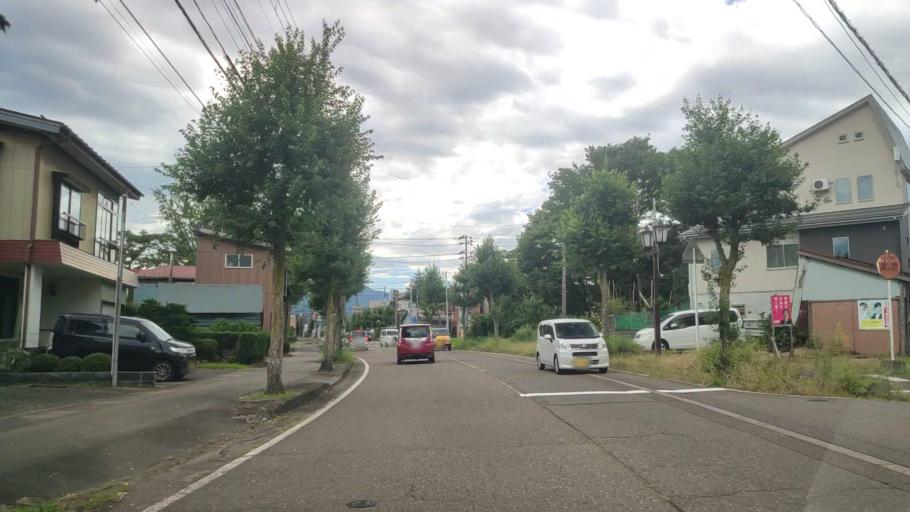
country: JP
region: Niigata
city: Arai
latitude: 37.0258
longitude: 138.2460
